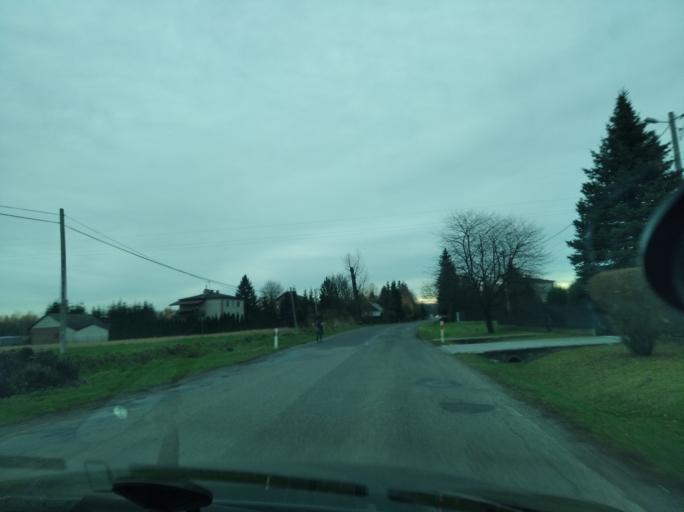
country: PL
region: Subcarpathian Voivodeship
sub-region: Powiat lancucki
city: Czarna
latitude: 50.0860
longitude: 22.1872
